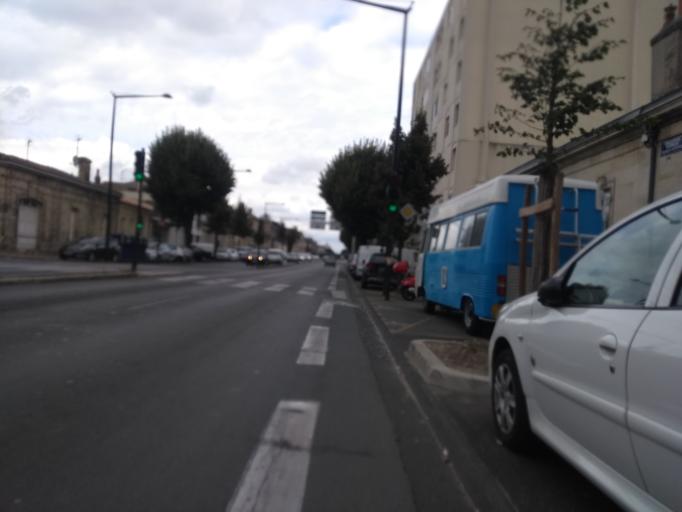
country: FR
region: Aquitaine
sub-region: Departement de la Gironde
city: Bordeaux
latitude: 44.8192
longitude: -0.5795
